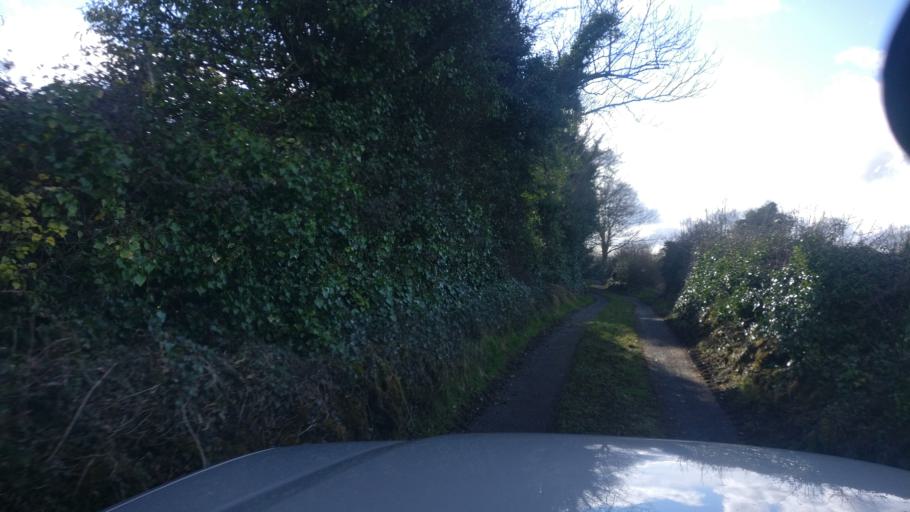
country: IE
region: Connaught
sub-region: County Galway
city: Loughrea
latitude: 53.1832
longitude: -8.4194
